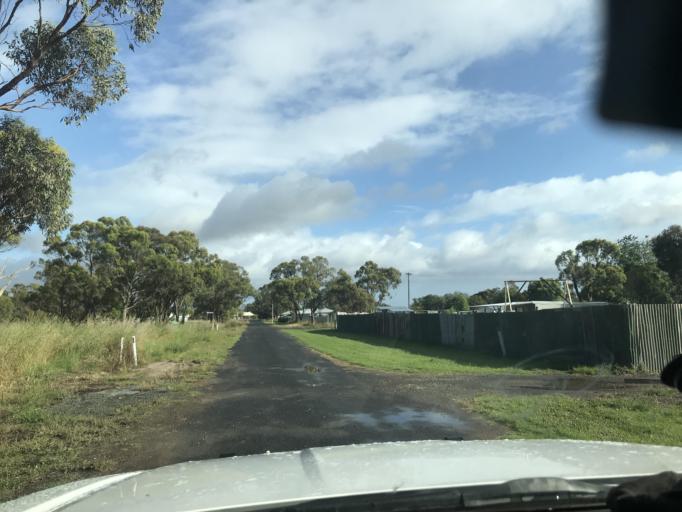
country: AU
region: Victoria
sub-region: Horsham
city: Horsham
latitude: -36.7224
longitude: 141.4715
